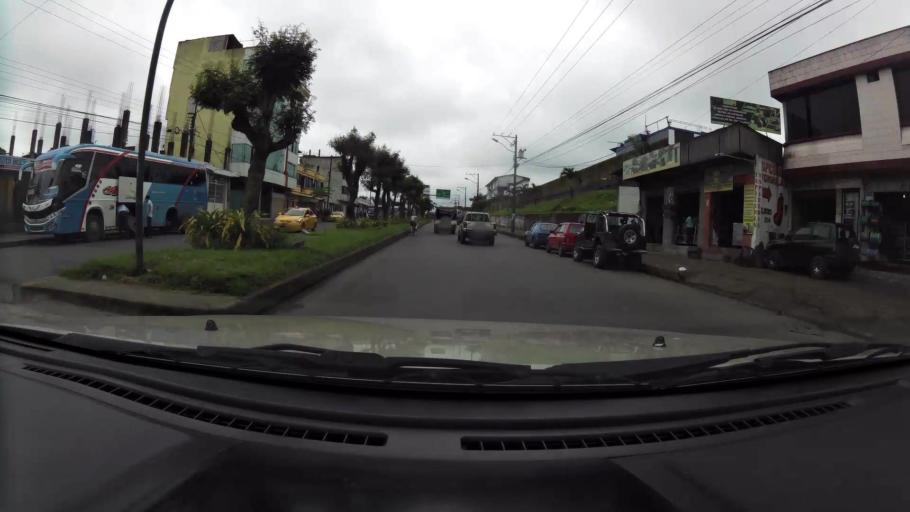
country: EC
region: Santo Domingo de los Tsachilas
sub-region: Canton Santo Domingo de los Colorados
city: Santo Domingo de los Colorados
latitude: -0.2411
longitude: -79.1702
